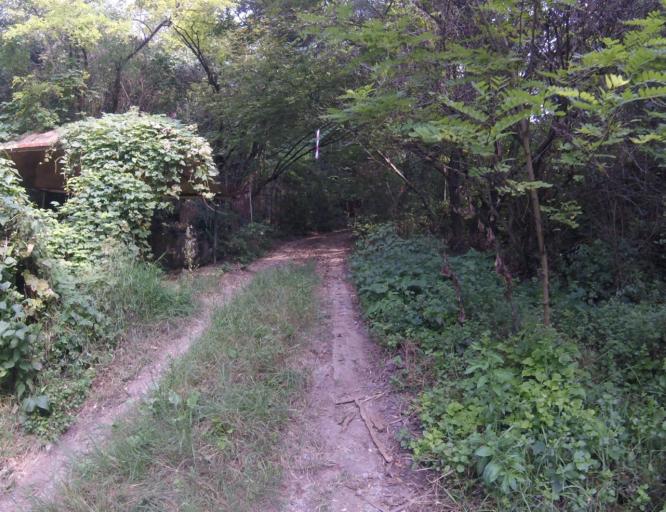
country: HU
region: Pest
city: Veroce
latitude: 47.8342
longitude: 19.0421
